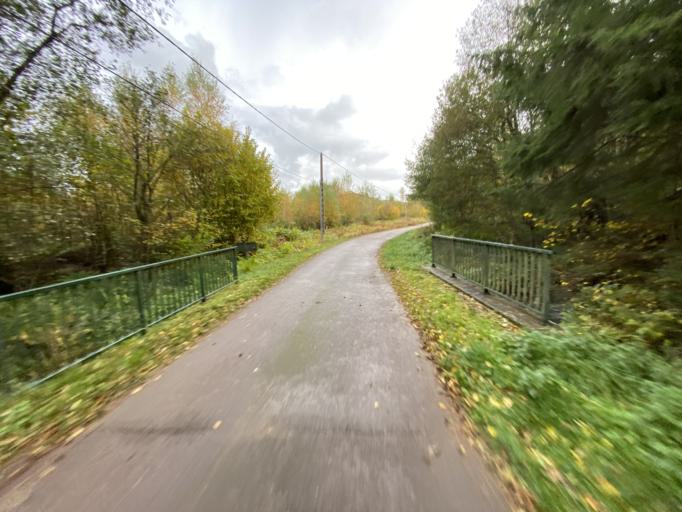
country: FR
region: Bourgogne
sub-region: Departement de la Cote-d'Or
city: Saulieu
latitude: 47.2958
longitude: 4.1246
